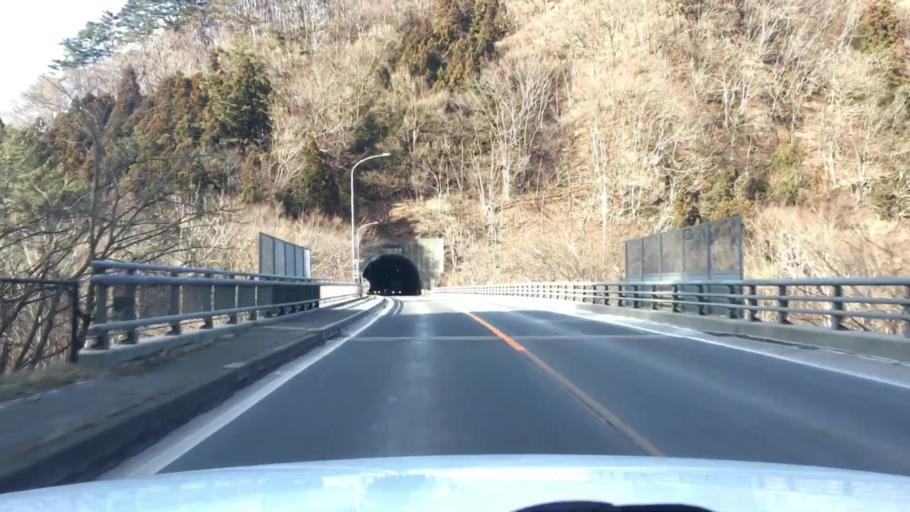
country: JP
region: Iwate
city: Tono
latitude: 39.6276
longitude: 141.6087
